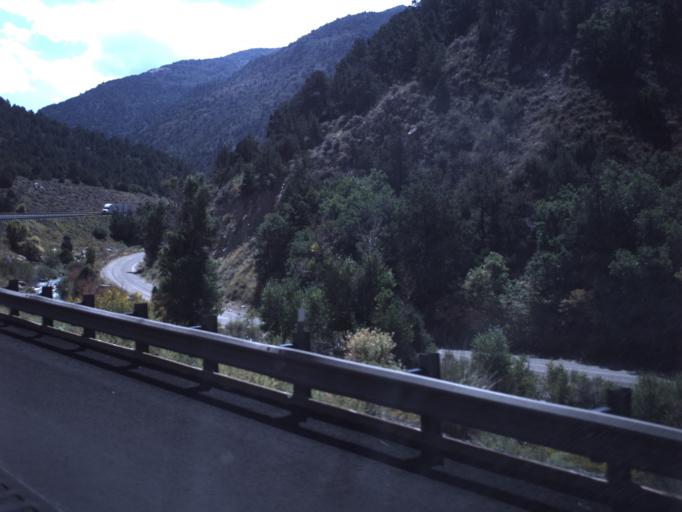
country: US
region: Utah
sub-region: Sevier County
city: Salina
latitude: 38.9044
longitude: -111.6353
